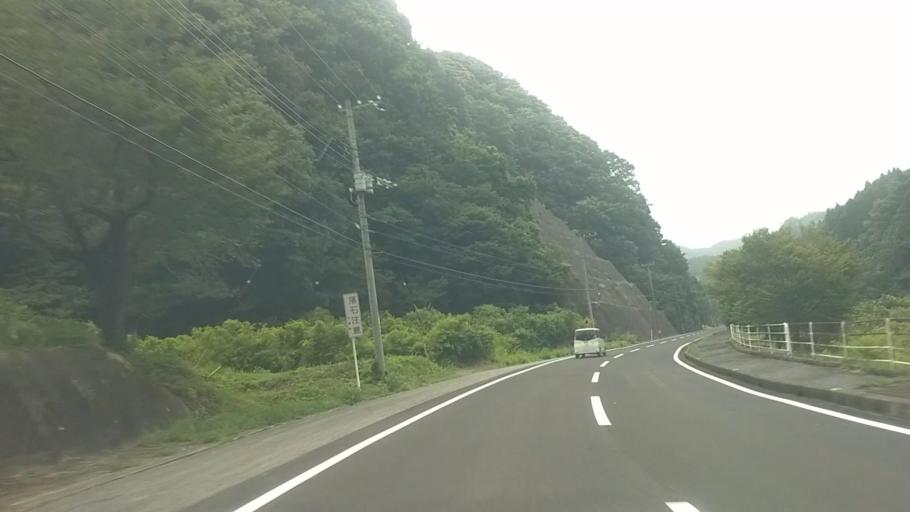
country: JP
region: Chiba
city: Kawaguchi
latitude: 35.2354
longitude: 140.1614
